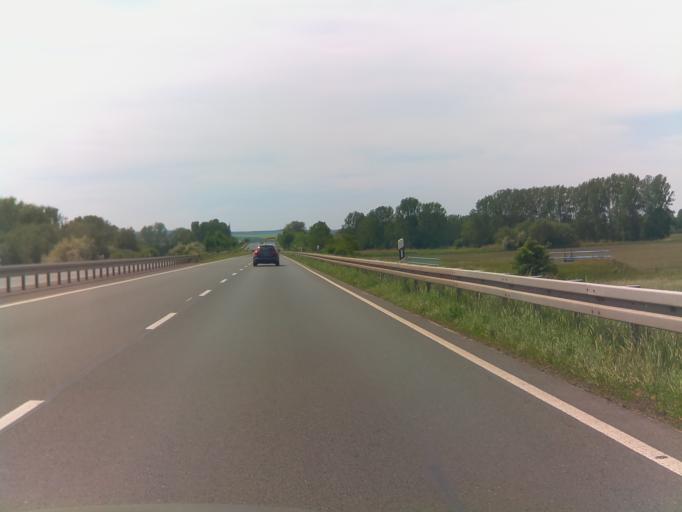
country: DE
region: Saxony-Anhalt
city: Egeln
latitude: 51.9481
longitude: 11.4246
